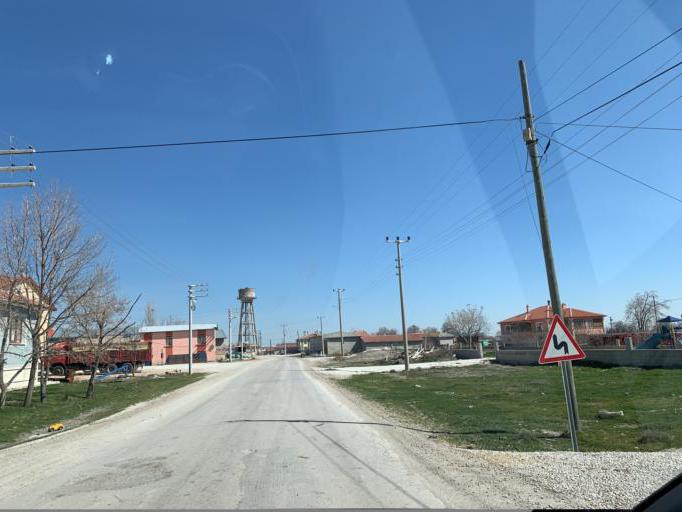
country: TR
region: Konya
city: Yarma
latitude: 37.7508
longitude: 32.8576
